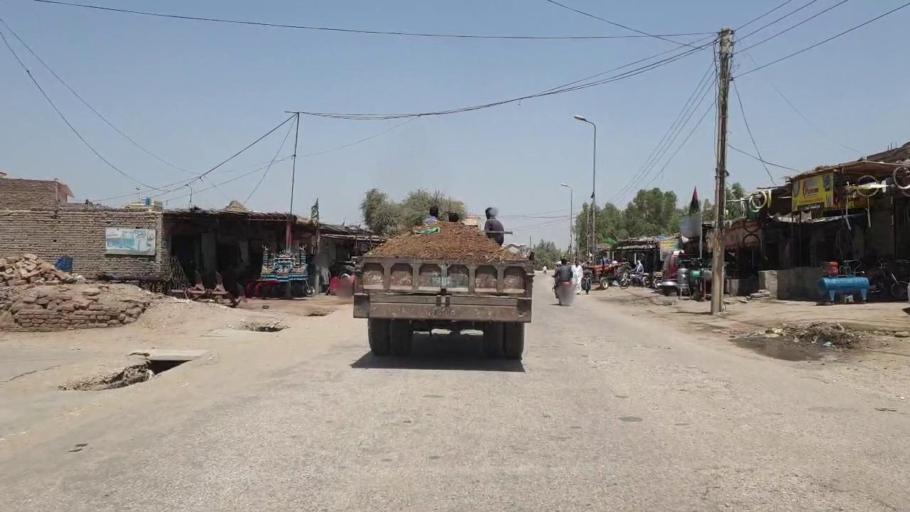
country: PK
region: Sindh
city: Adilpur
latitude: 27.9387
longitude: 69.3194
